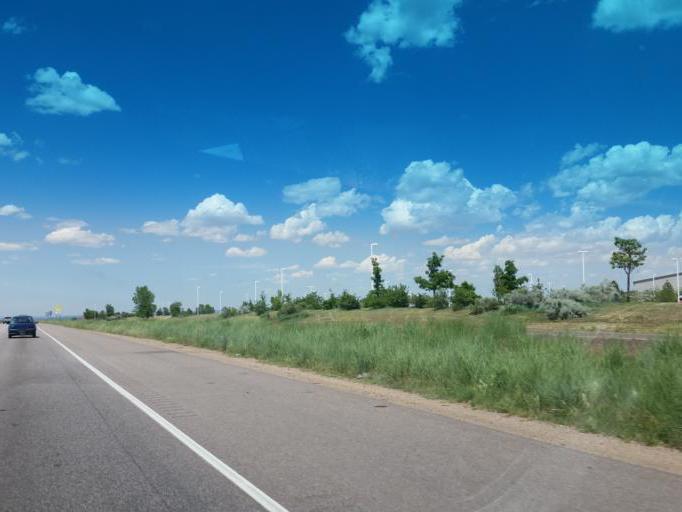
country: US
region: Colorado
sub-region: Larimer County
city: Loveland
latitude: 40.4436
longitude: -104.9920
